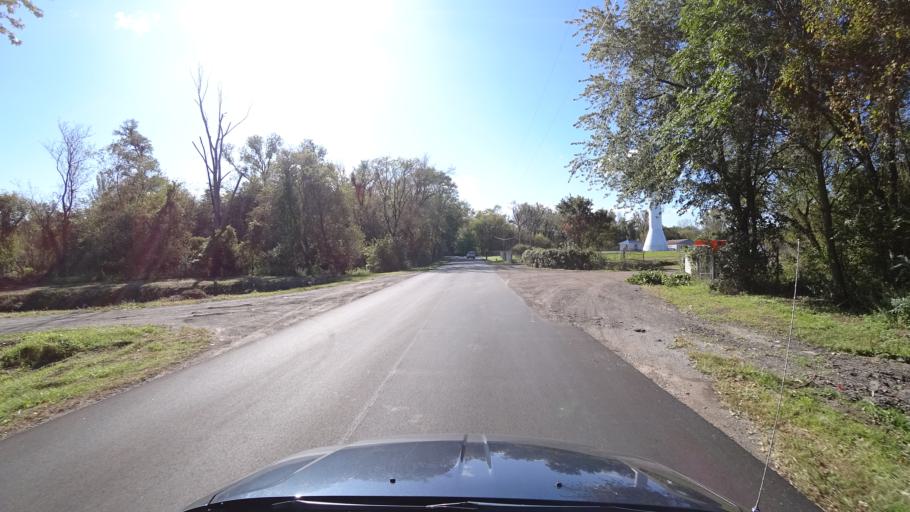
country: US
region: Indiana
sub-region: LaPorte County
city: Michigan City
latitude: 41.6970
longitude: -86.9140
